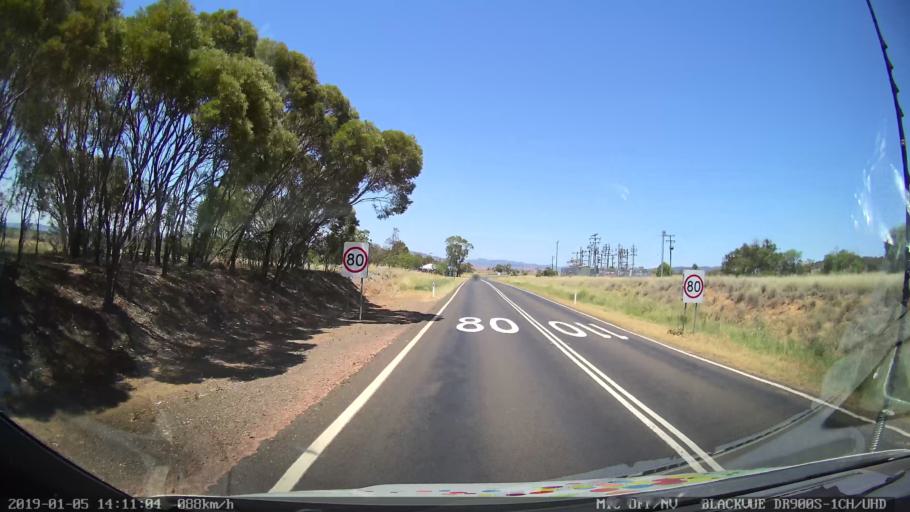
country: AU
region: New South Wales
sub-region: Gunnedah
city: Gunnedah
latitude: -31.2443
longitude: 150.4528
